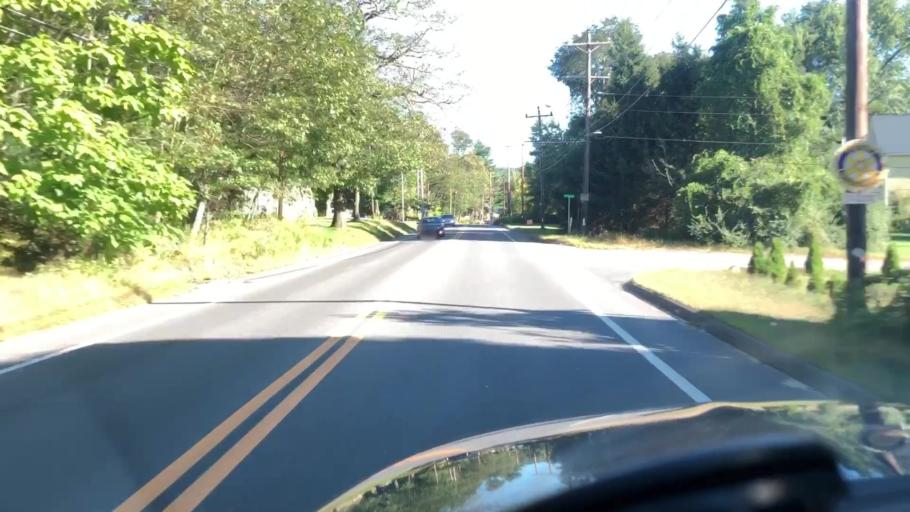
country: US
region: Massachusetts
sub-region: Hampden County
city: Palmer
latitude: 42.1426
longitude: -72.3127
